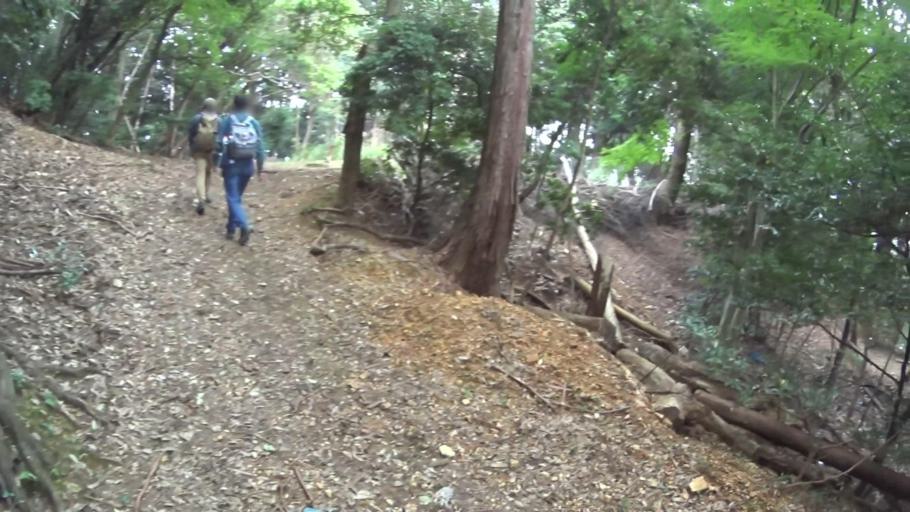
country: JP
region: Osaka
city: Kishiwada
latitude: 34.5010
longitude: 135.3336
